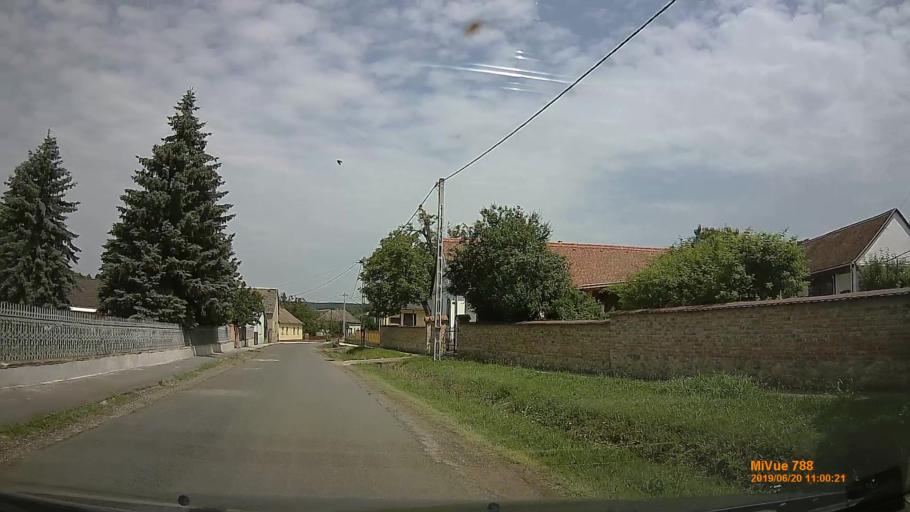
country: HU
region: Baranya
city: Mecseknadasd
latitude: 46.1716
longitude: 18.5129
